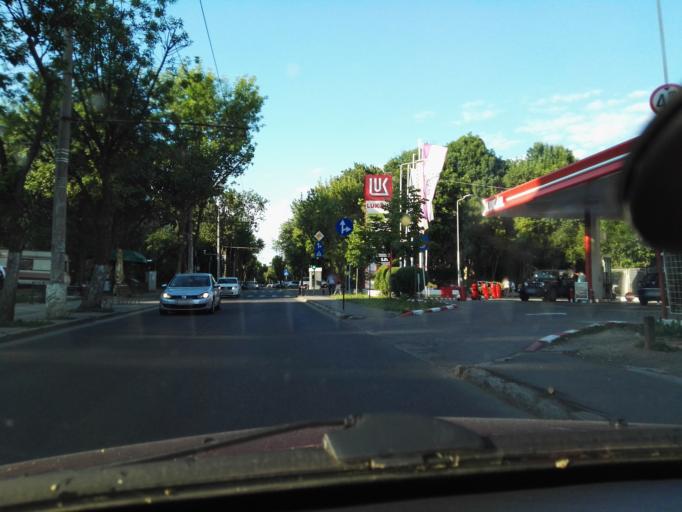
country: RO
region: Bucuresti
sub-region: Municipiul Bucuresti
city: Bucuresti
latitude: 44.3843
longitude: 26.1012
